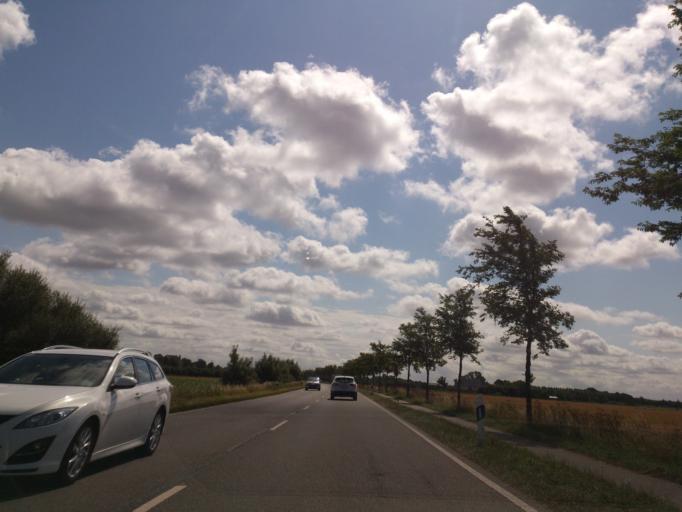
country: DE
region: Schleswig-Holstein
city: Grothusenkoog
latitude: 54.3006
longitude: 8.7721
